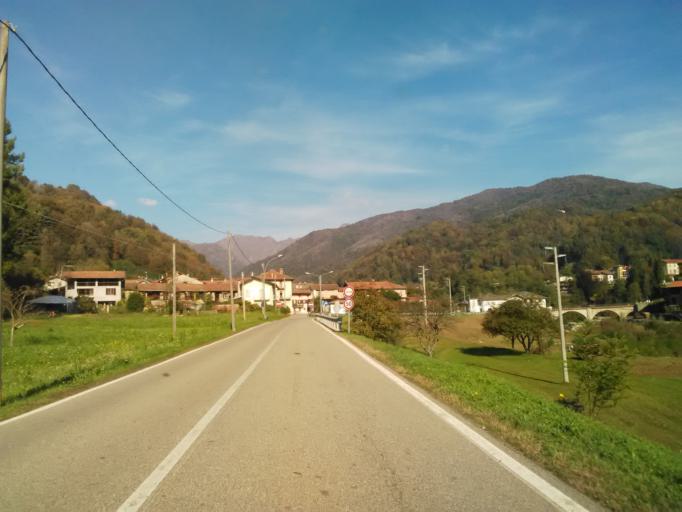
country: IT
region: Piedmont
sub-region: Provincia di Vercelli
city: Postua
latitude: 45.7092
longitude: 8.2293
